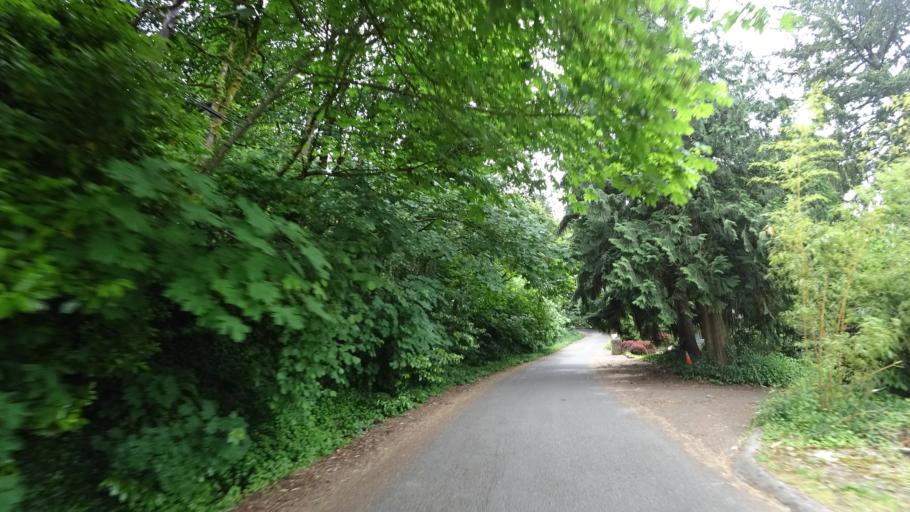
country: US
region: Oregon
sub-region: Multnomah County
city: Lents
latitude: 45.5014
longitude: -122.5576
